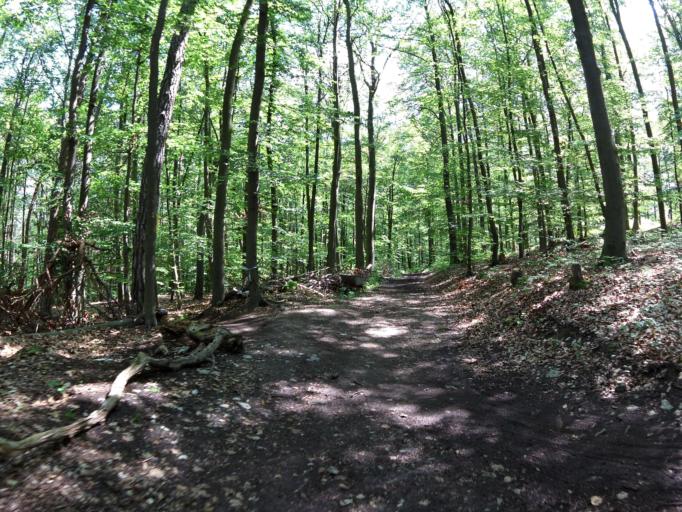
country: DE
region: Bavaria
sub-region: Regierungsbezirk Unterfranken
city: Eibelstadt
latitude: 49.7322
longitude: 10.0033
